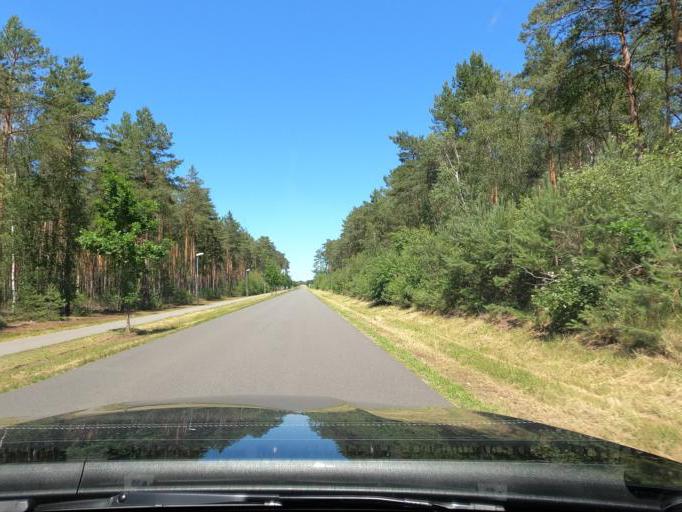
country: DE
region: Lower Saxony
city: Lachendorf
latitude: 52.6106
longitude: 10.2557
